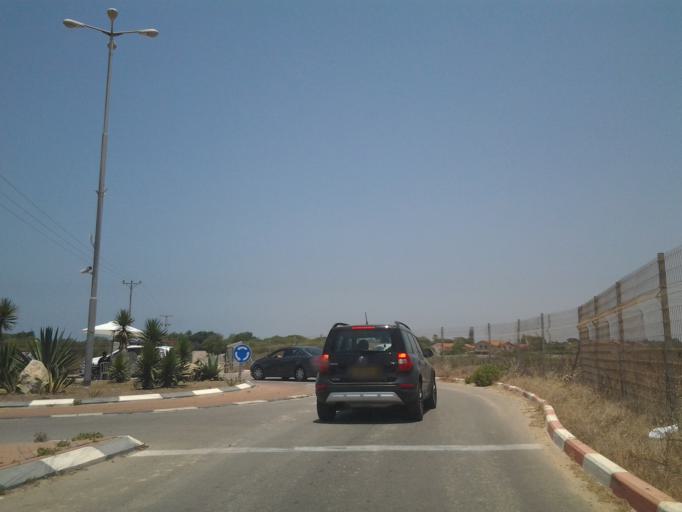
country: IL
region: Haifa
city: Qesarya
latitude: 32.4875
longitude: 34.8936
